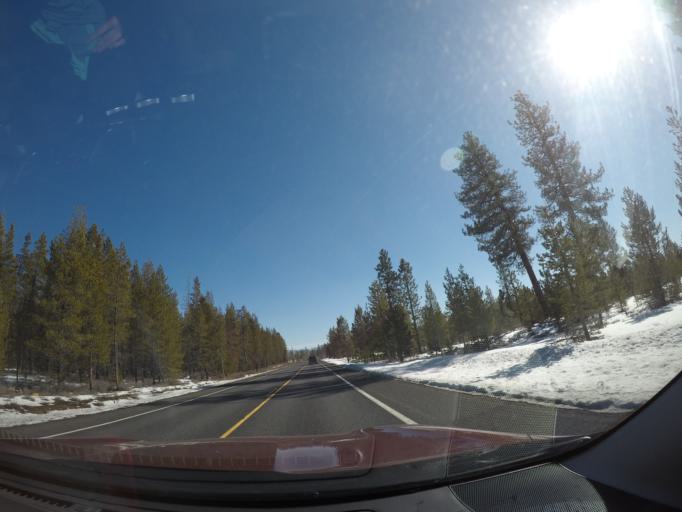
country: US
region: Oregon
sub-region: Deschutes County
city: Three Rivers
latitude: 43.8585
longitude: -121.5251
